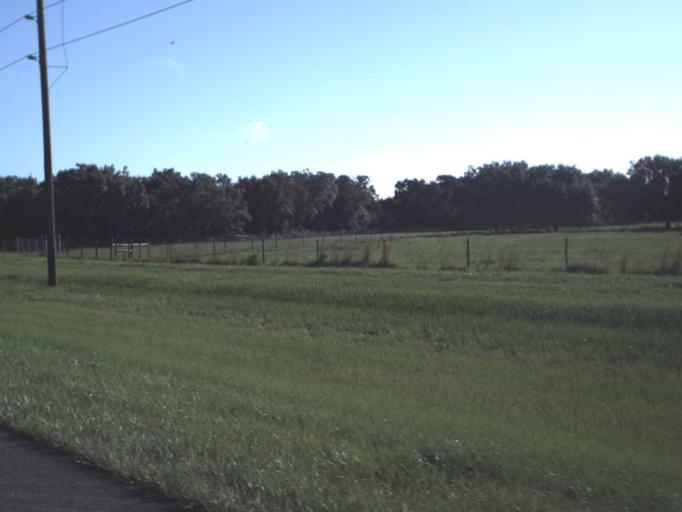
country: US
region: Florida
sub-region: DeSoto County
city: Nocatee
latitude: 27.1472
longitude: -81.8920
